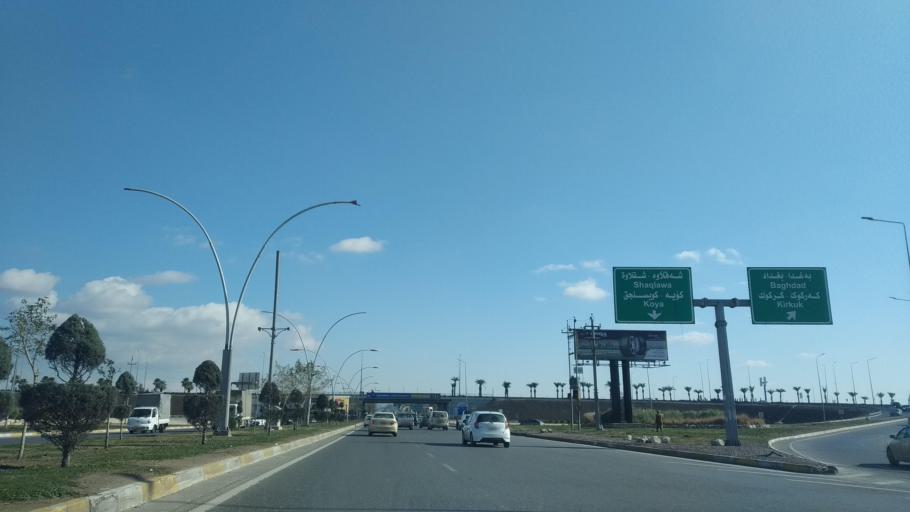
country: IQ
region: Arbil
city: Erbil
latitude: 36.1968
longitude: 44.0653
